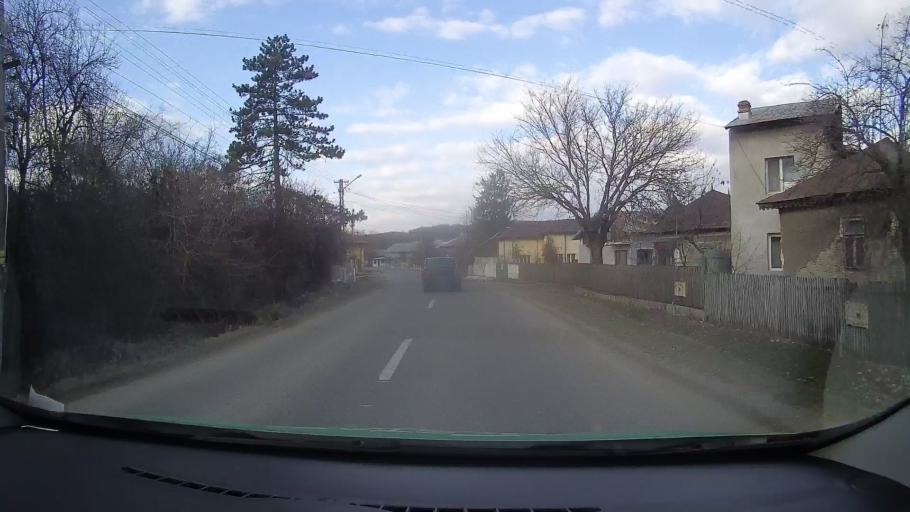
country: RO
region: Dambovita
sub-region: Comuna Gura Ocnitei
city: Gura Ocnitei
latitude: 44.9377
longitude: 25.5637
